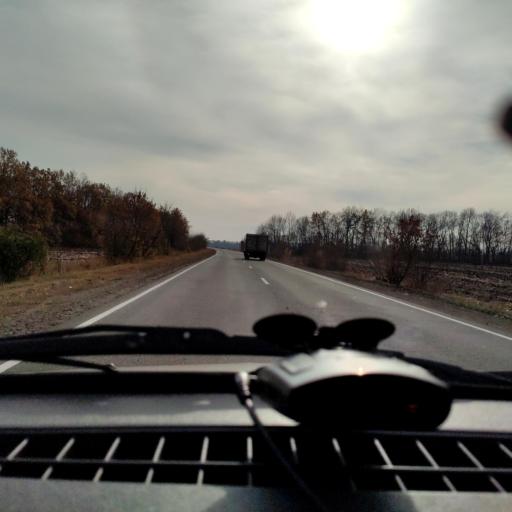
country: RU
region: Voronezj
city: Shilovo
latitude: 51.4434
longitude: 38.9950
